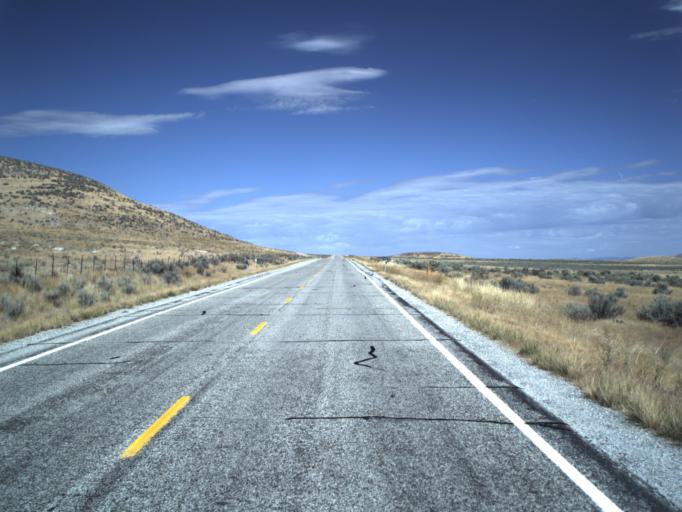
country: US
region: Utah
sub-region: Box Elder County
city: Tremonton
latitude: 41.6988
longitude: -112.4465
